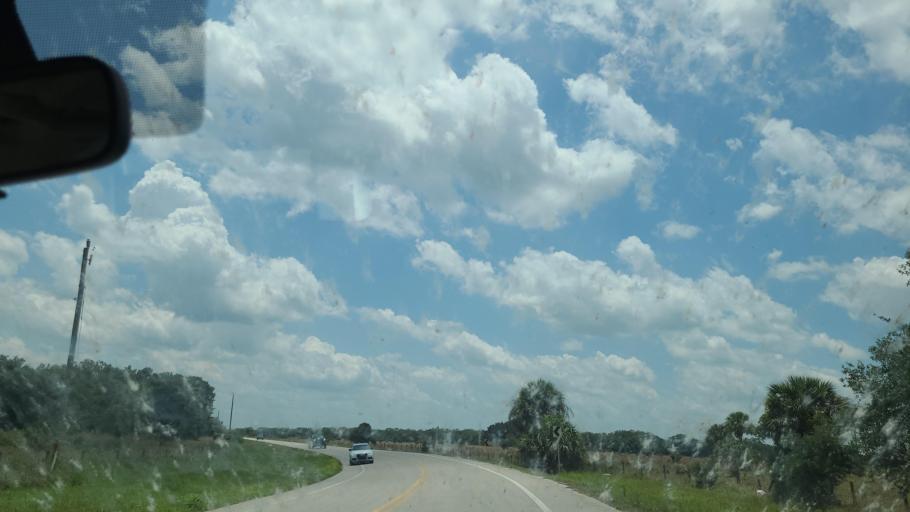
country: US
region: Florida
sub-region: Glades County
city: Buckhead Ridge
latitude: 27.1449
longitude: -81.0941
